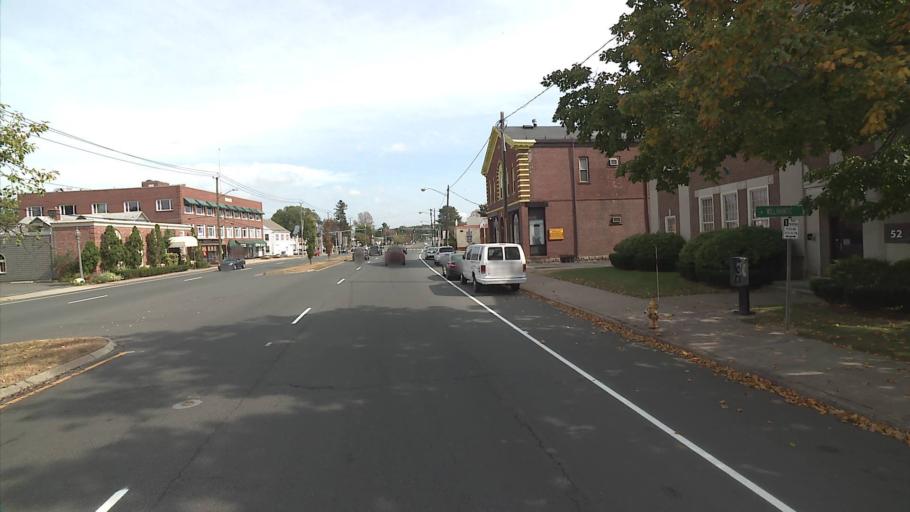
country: US
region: Connecticut
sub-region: Hartford County
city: Manchester
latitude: 41.7761
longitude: -72.5208
